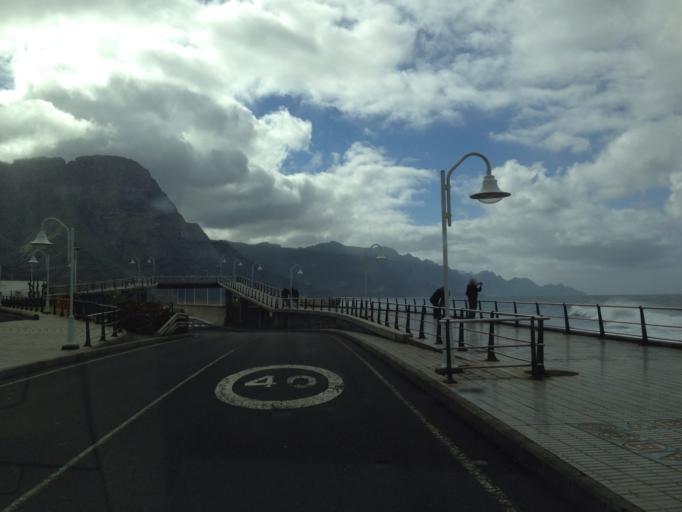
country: ES
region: Canary Islands
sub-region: Provincia de Las Palmas
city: Agaete
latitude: 28.1034
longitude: -15.7125
